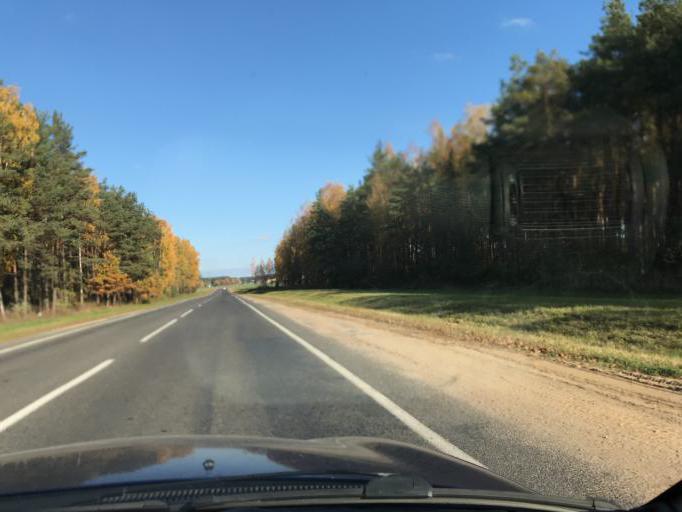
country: BY
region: Grodnenskaya
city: Lida
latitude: 53.9454
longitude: 25.2460
